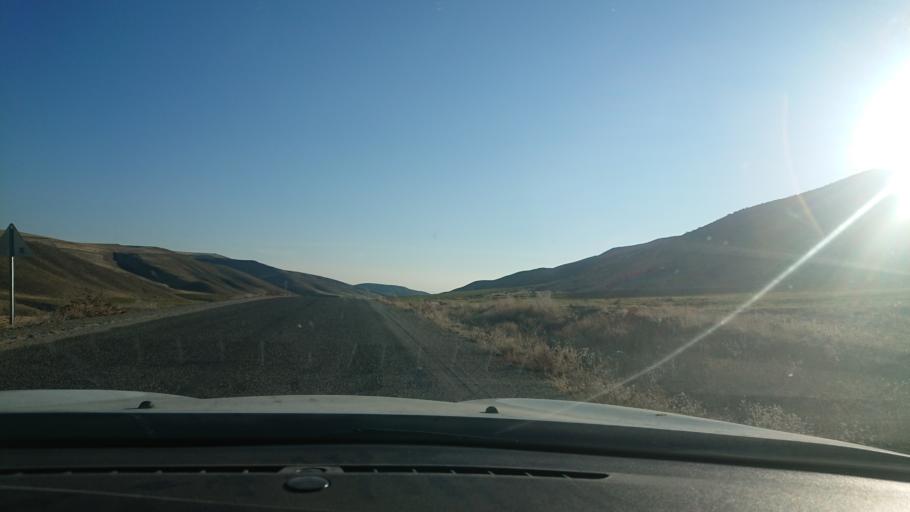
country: TR
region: Aksaray
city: Acipinar
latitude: 38.7102
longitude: 33.7583
